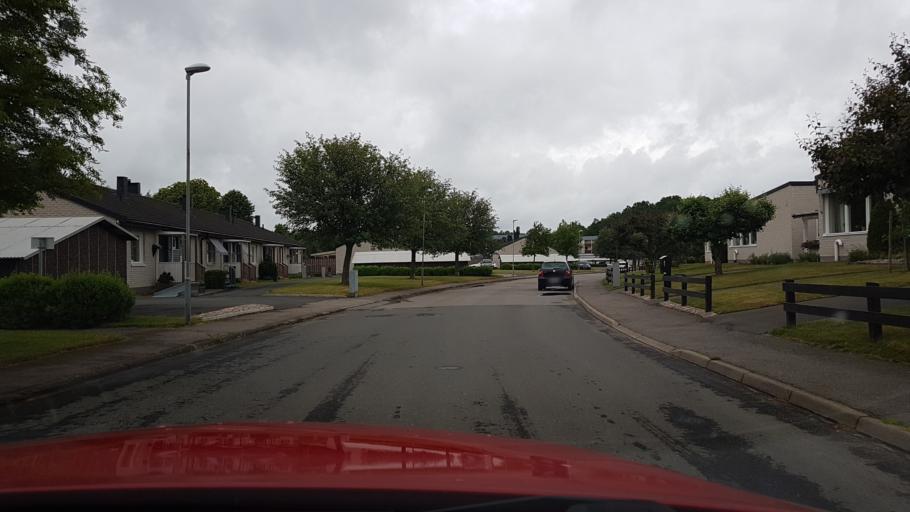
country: SE
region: Vaestra Goetaland
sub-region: Skovde Kommun
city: Skultorp
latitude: 58.3668
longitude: 13.8244
